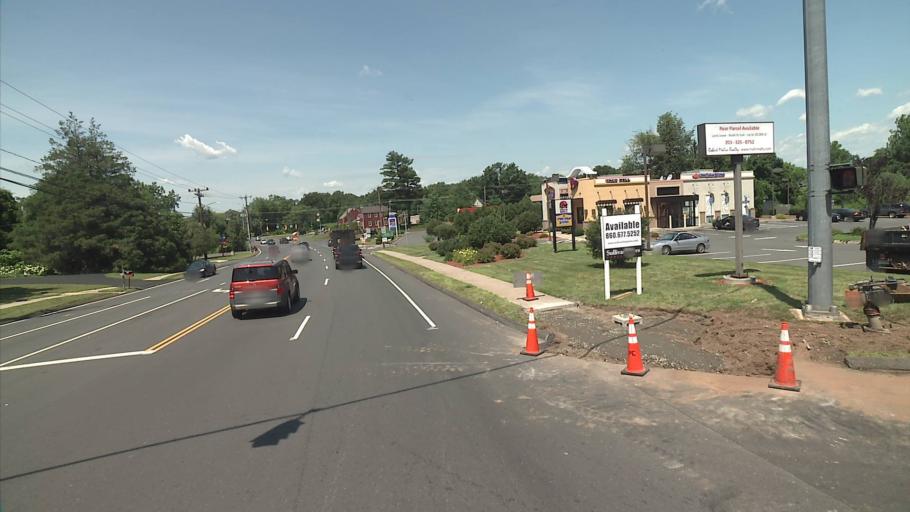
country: US
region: Connecticut
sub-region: Hartford County
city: Plainville
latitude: 41.6777
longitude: -72.8452
